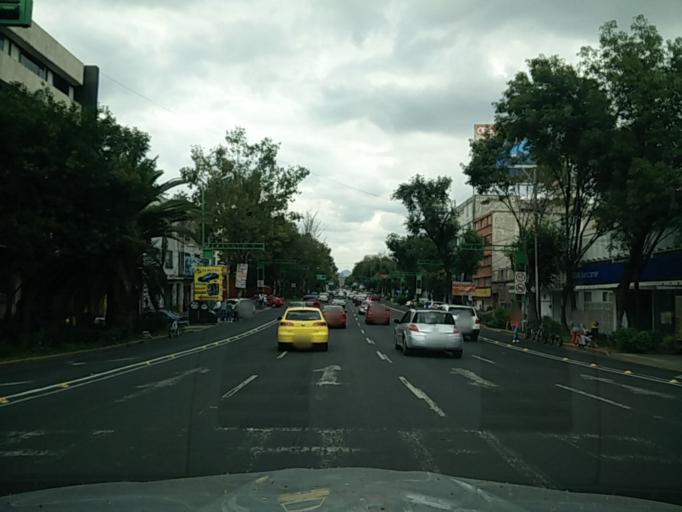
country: MX
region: Mexico City
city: Benito Juarez
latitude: 19.4040
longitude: -99.1450
